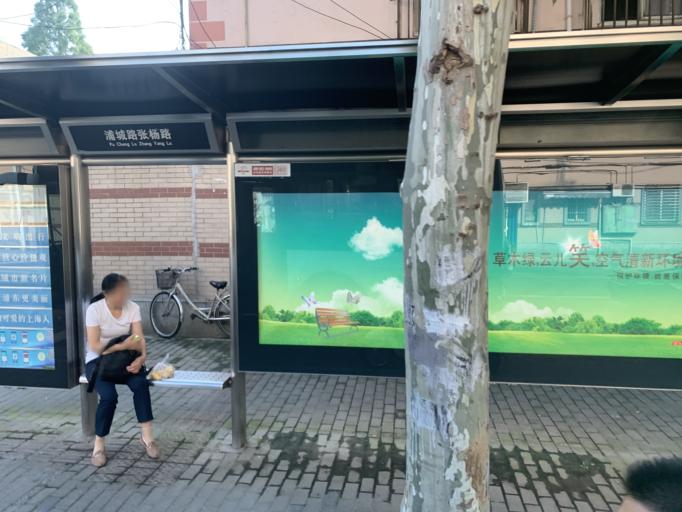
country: CN
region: Shanghai Shi
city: Pudong
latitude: 31.2268
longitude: 121.5097
